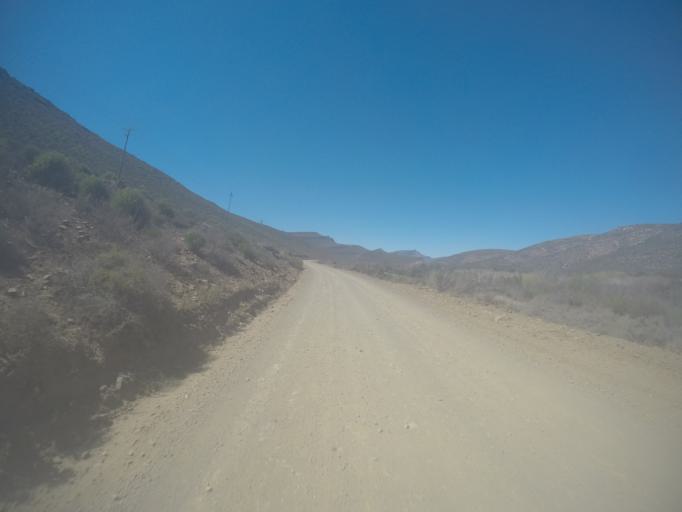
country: ZA
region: Western Cape
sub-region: West Coast District Municipality
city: Clanwilliam
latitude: -32.5123
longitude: 19.3449
